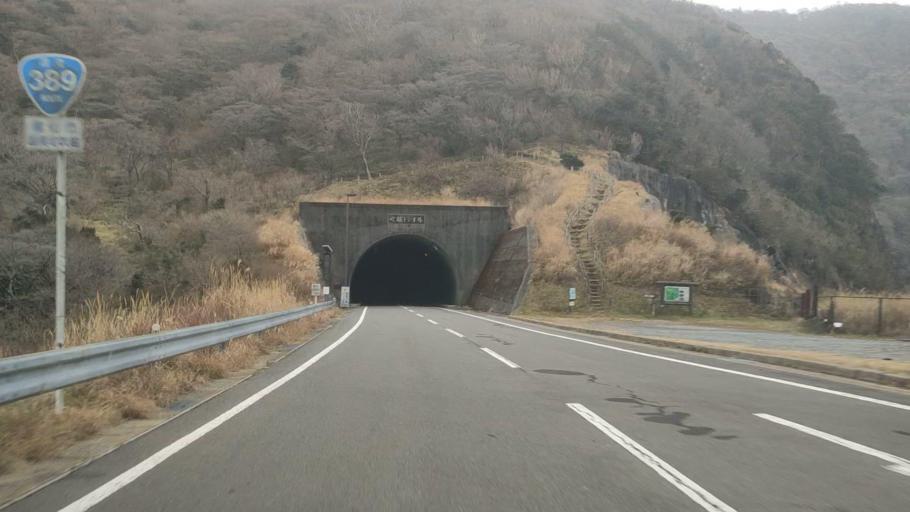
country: JP
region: Nagasaki
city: Shimabara
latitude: 32.7633
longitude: 130.2750
